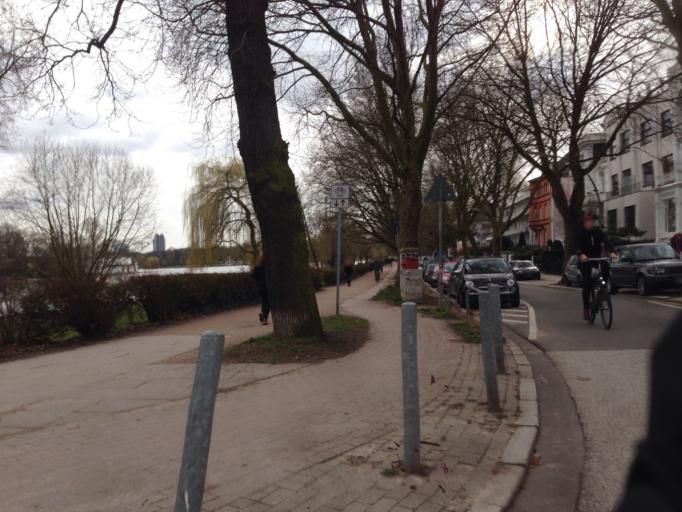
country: DE
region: Hamburg
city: Hamburg
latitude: 53.5783
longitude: 10.0095
